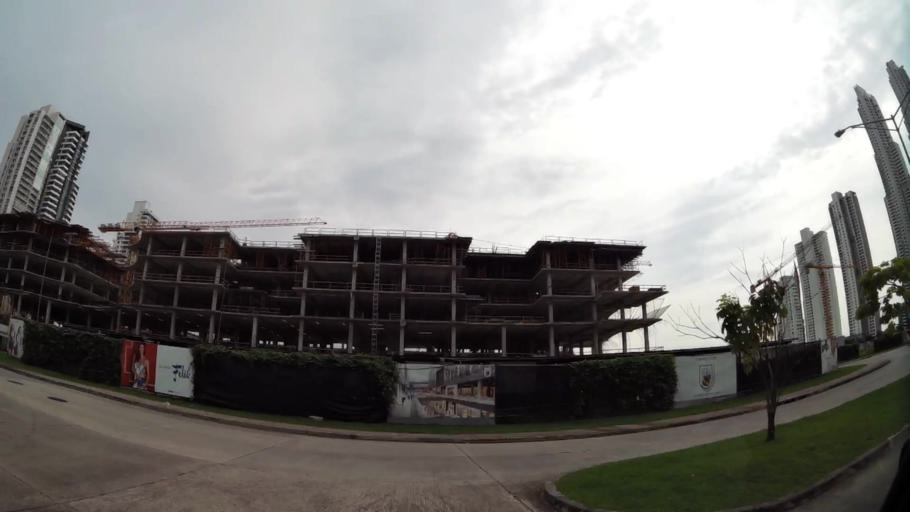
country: PA
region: Panama
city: San Miguelito
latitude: 9.0144
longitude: -79.4658
